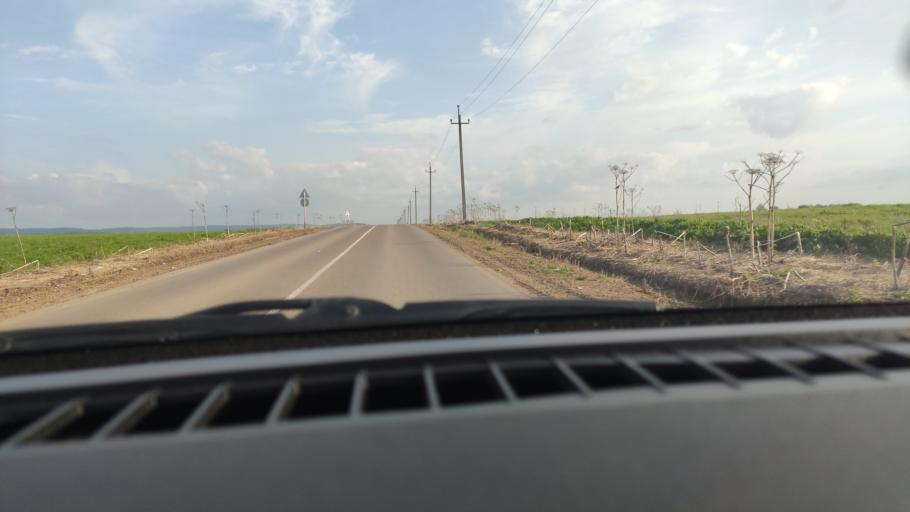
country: RU
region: Perm
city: Kultayevo
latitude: 57.8951
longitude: 55.9914
